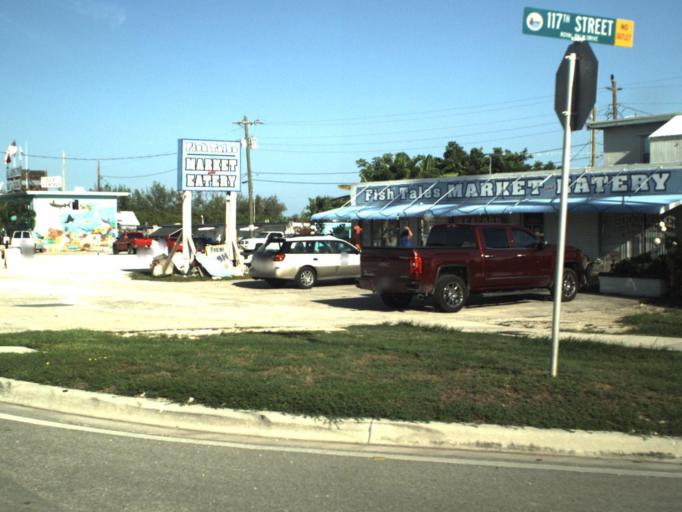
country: US
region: Florida
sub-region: Monroe County
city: Marathon
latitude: 24.7299
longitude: -81.0314
